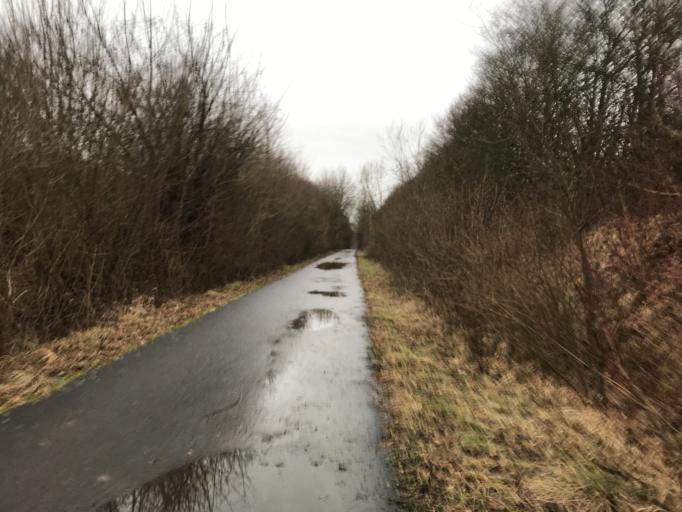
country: DE
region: Rheinland-Pfalz
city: Mommenheim
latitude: 49.8716
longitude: 8.2717
